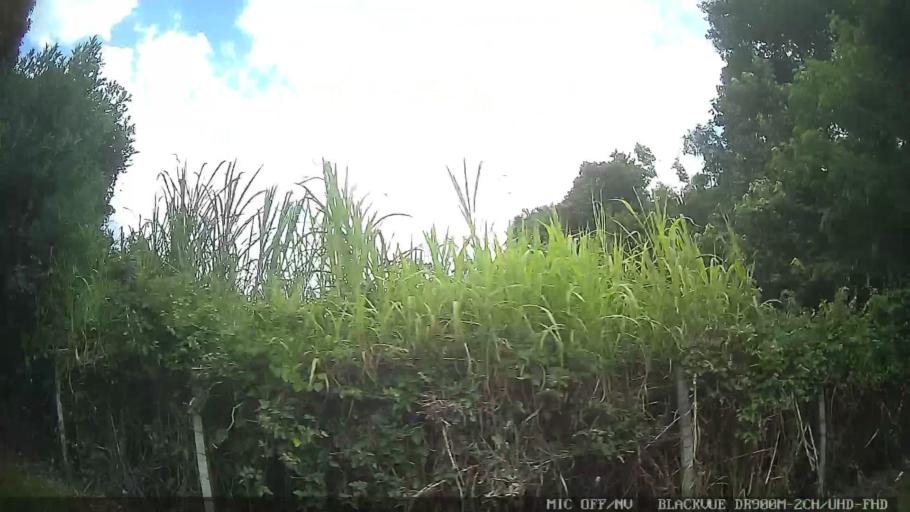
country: BR
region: Sao Paulo
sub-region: Jarinu
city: Jarinu
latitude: -23.0741
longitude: -46.6423
